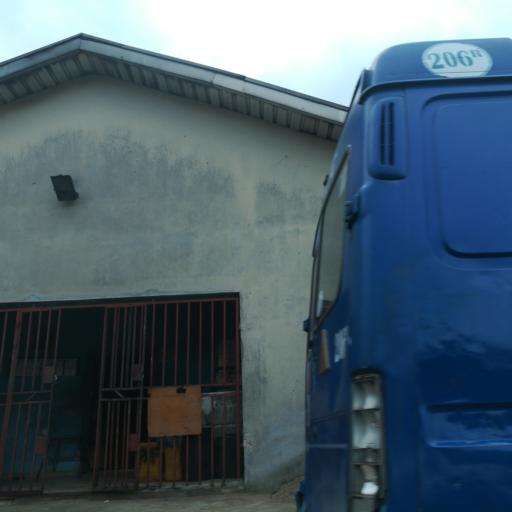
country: NG
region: Rivers
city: Port Harcourt
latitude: 4.8079
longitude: 7.0500
